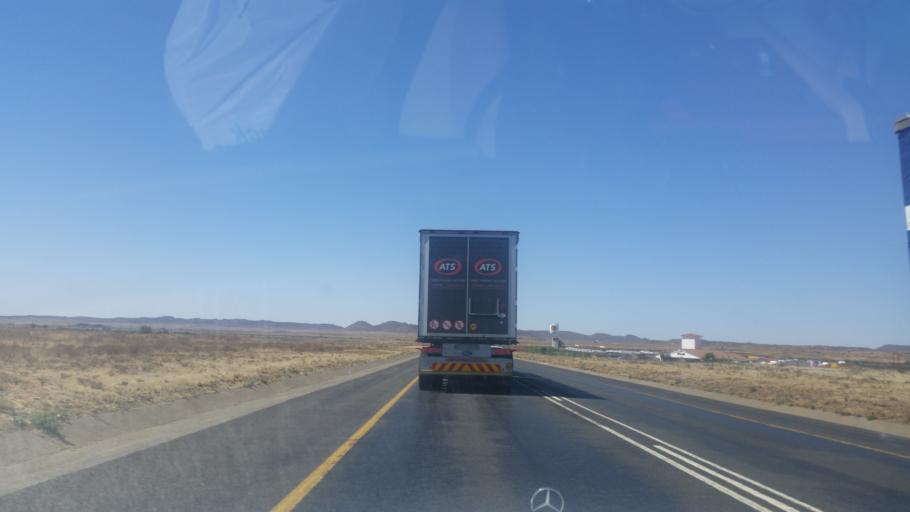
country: ZA
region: Northern Cape
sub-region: Pixley ka Seme District Municipality
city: Colesberg
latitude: -30.7018
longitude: 25.1225
